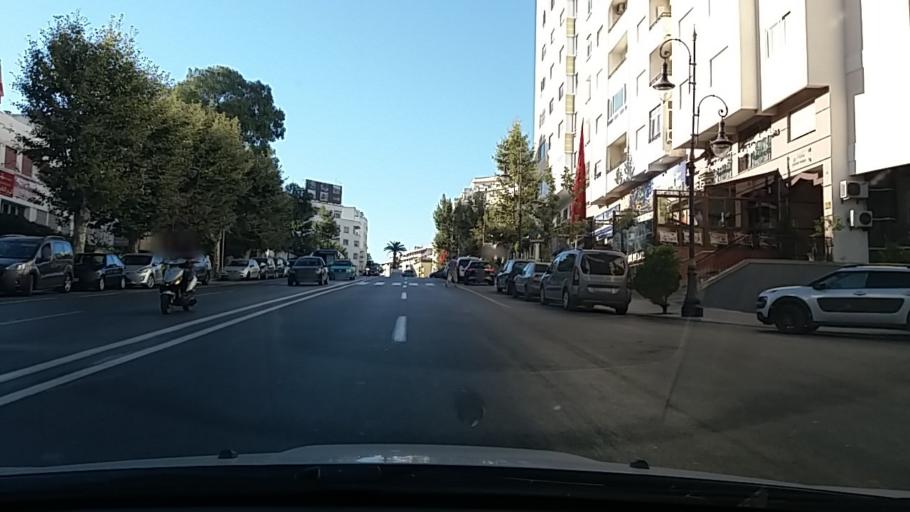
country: MA
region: Tanger-Tetouan
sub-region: Tanger-Assilah
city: Tangier
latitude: 35.7799
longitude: -5.8202
